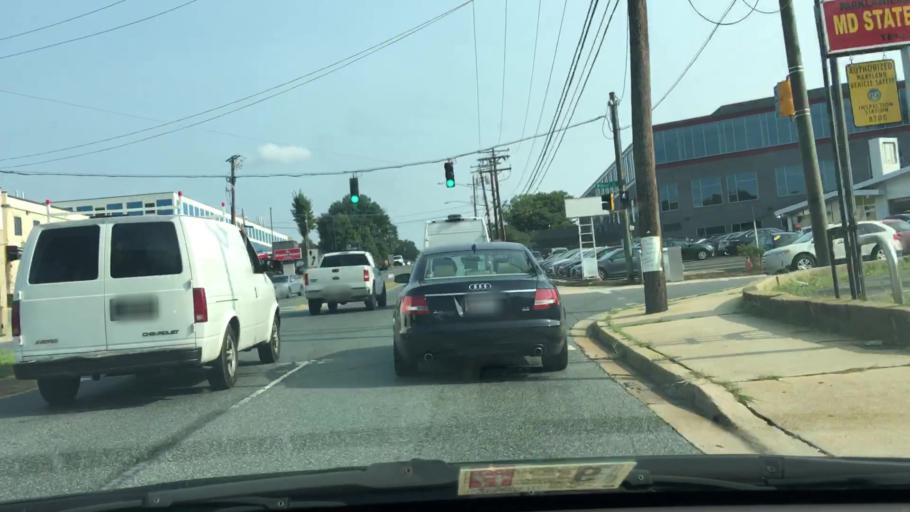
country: US
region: Maryland
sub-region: Montgomery County
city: North Bethesda
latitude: 39.0611
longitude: -77.1119
